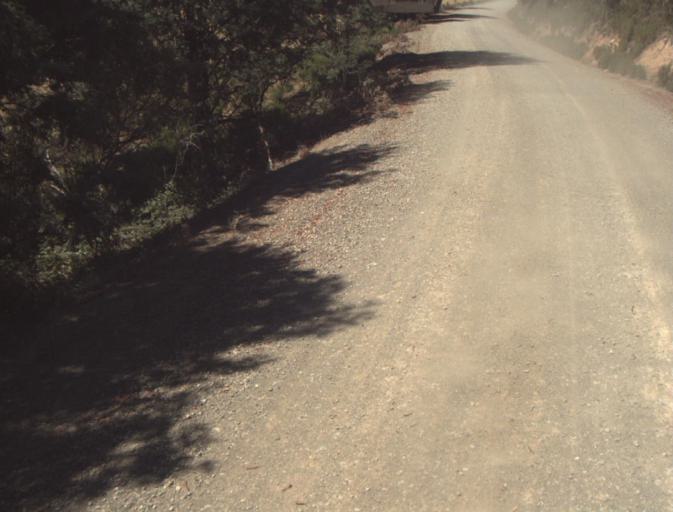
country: AU
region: Tasmania
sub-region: Dorset
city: Scottsdale
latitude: -41.3029
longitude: 147.3655
